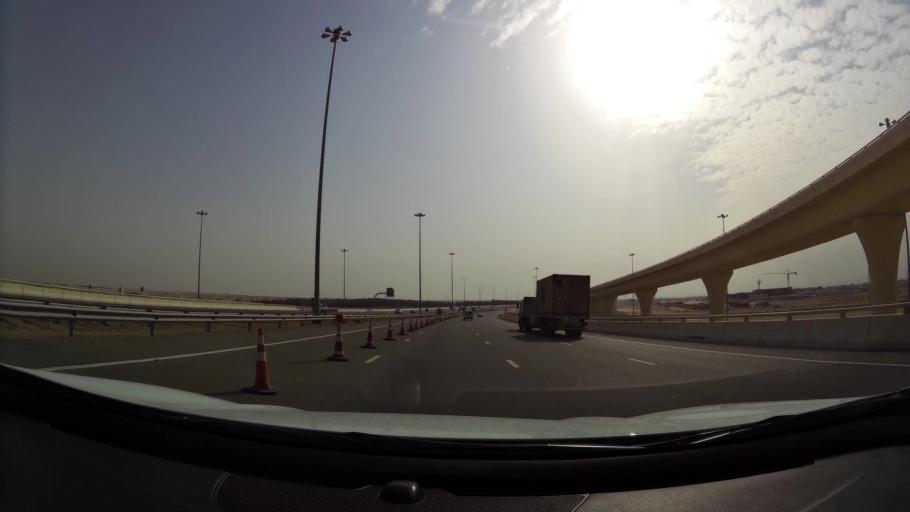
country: AE
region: Abu Dhabi
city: Abu Dhabi
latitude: 24.3070
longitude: 54.5997
